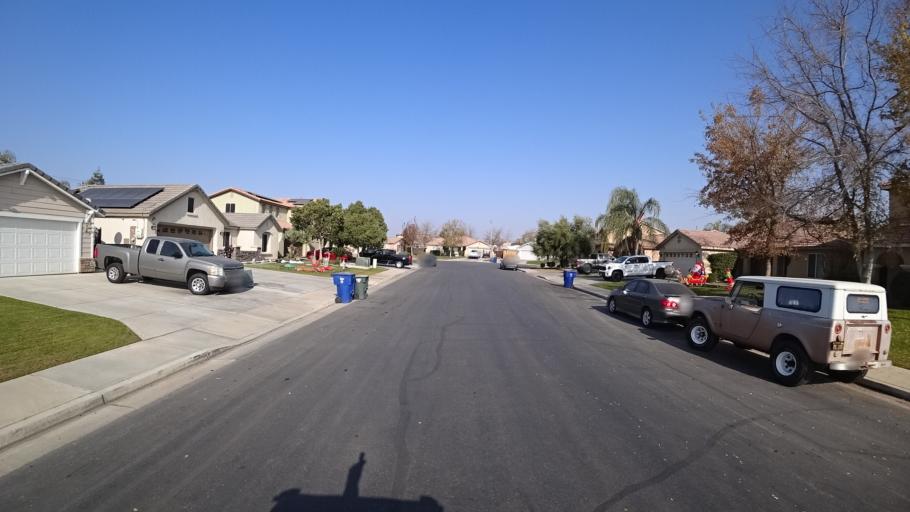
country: US
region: California
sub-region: Kern County
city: Greenacres
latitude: 35.4186
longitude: -119.1270
